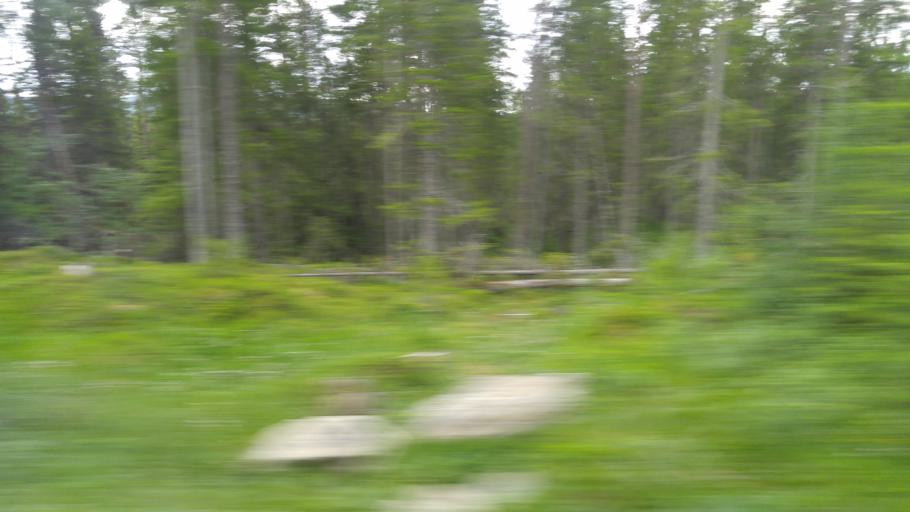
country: NO
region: Nord-Trondelag
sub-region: Meraker
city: Meraker
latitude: 63.4019
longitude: 11.8333
